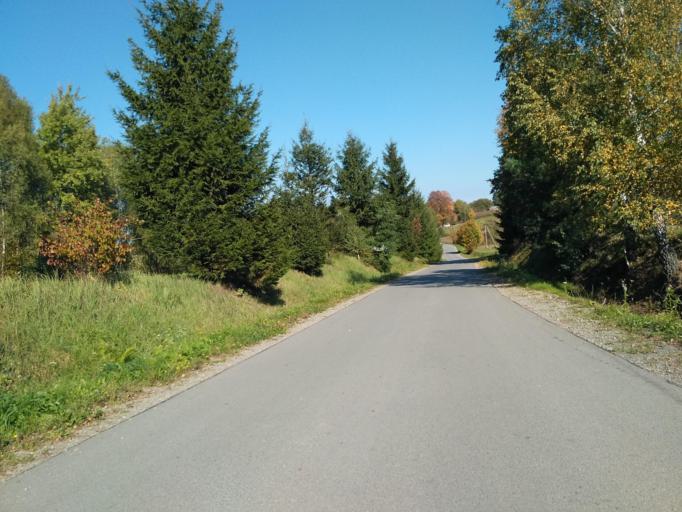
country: PL
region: Subcarpathian Voivodeship
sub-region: Powiat debicki
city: Brzostek
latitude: 49.9474
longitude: 21.3825
